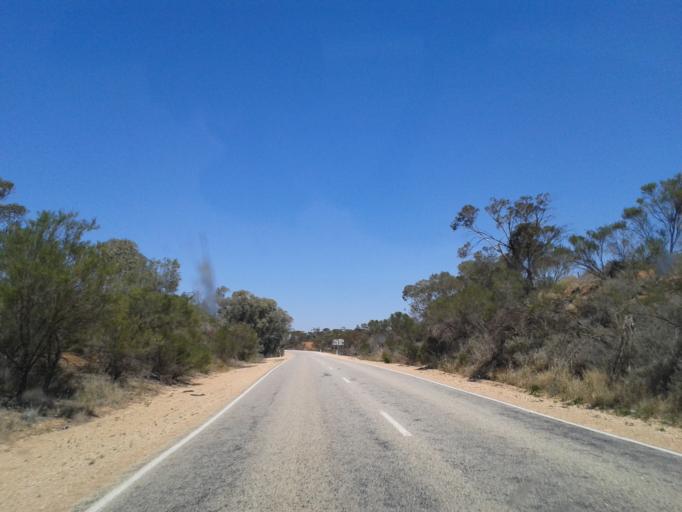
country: AU
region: Victoria
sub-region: Swan Hill
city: Swan Hill
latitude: -34.7464
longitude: 143.1851
